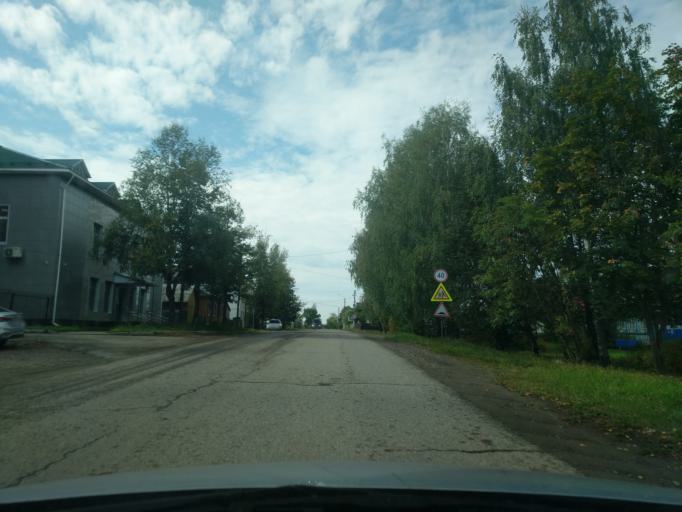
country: RU
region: Kostroma
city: Sudislavl'
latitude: 57.8809
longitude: 41.7175
